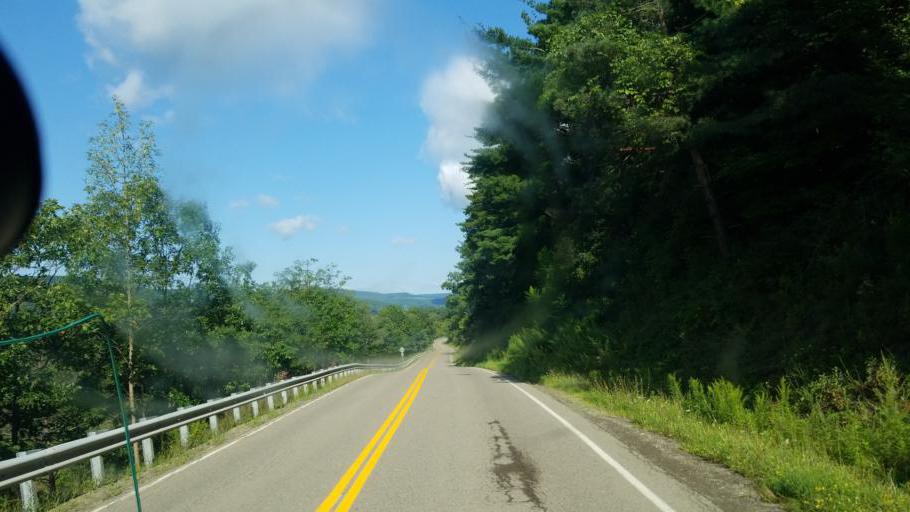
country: US
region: New York
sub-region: Steuben County
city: Canisteo
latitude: 42.2697
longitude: -77.5893
